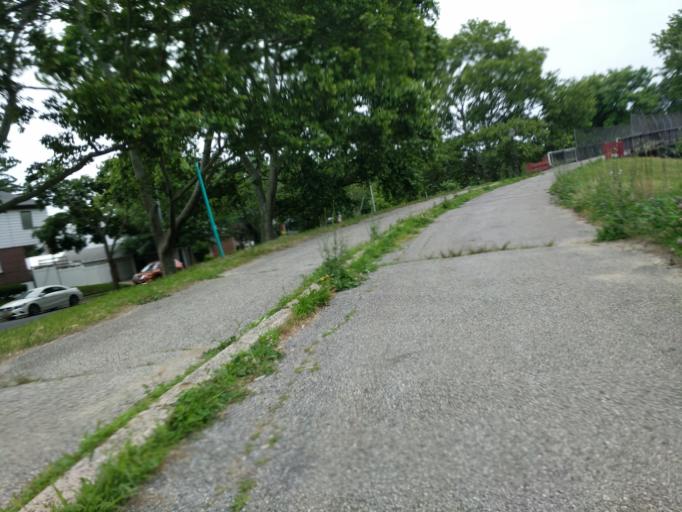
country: US
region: New York
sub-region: Queens County
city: Jamaica
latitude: 40.7433
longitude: -73.7812
